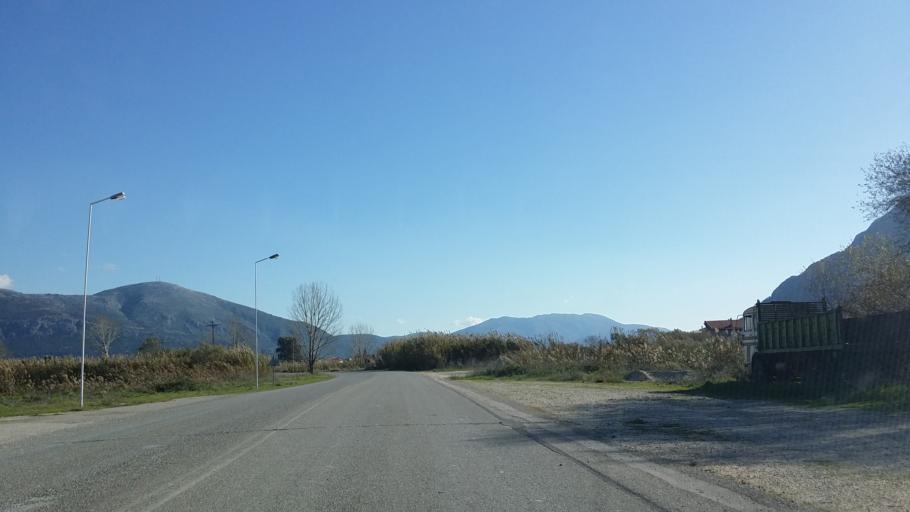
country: GR
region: West Greece
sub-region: Nomos Aitolias kai Akarnanias
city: Kandila
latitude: 38.6756
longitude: 20.9411
